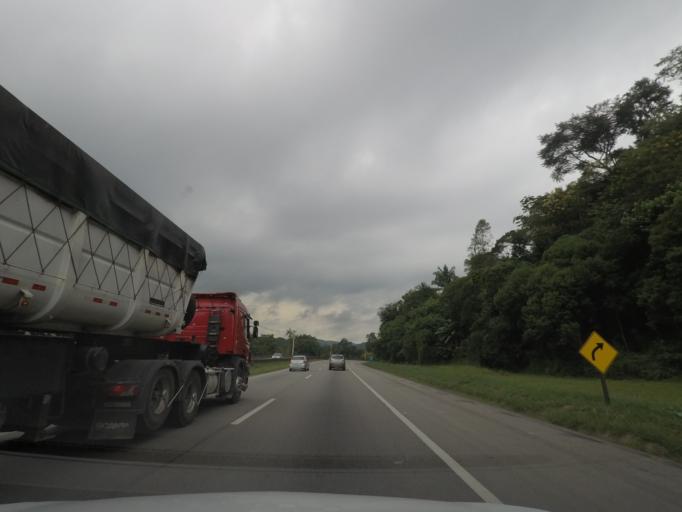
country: BR
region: Sao Paulo
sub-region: Miracatu
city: Miracatu
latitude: -24.1308
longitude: -47.2714
